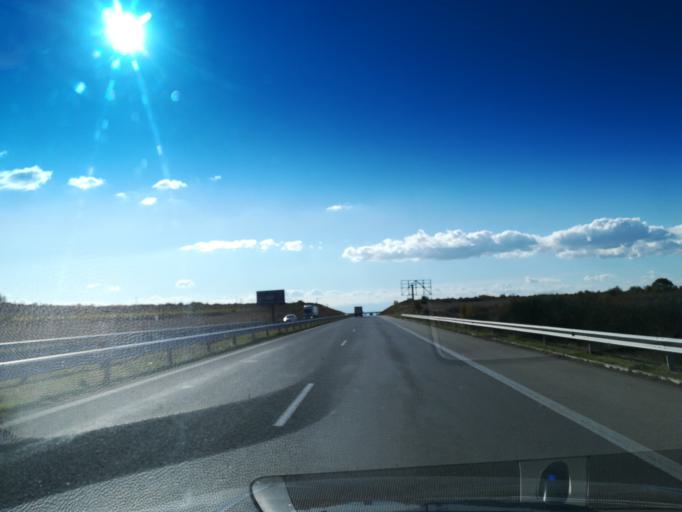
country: BG
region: Stara Zagora
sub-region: Obshtina Chirpan
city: Chirpan
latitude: 42.2320
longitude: 25.3580
